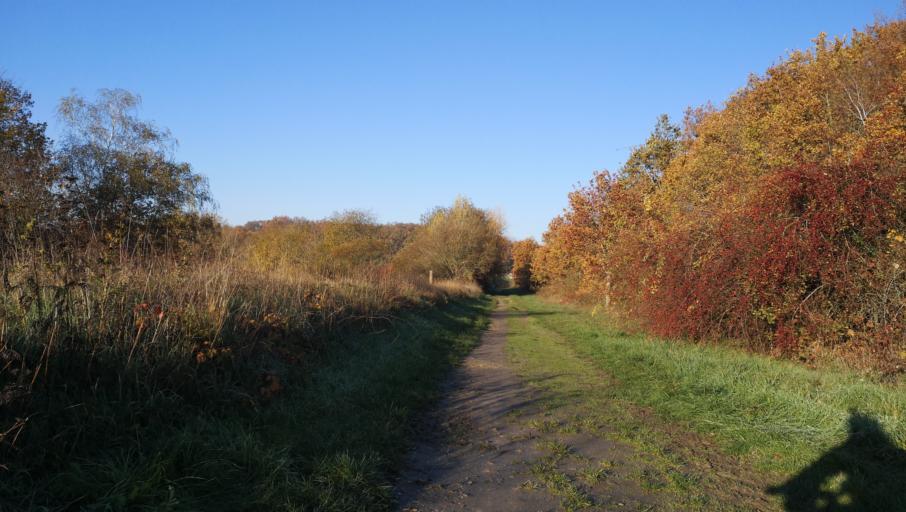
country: FR
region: Centre
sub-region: Departement du Loiret
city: Saran
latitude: 47.9415
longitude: 1.8652
